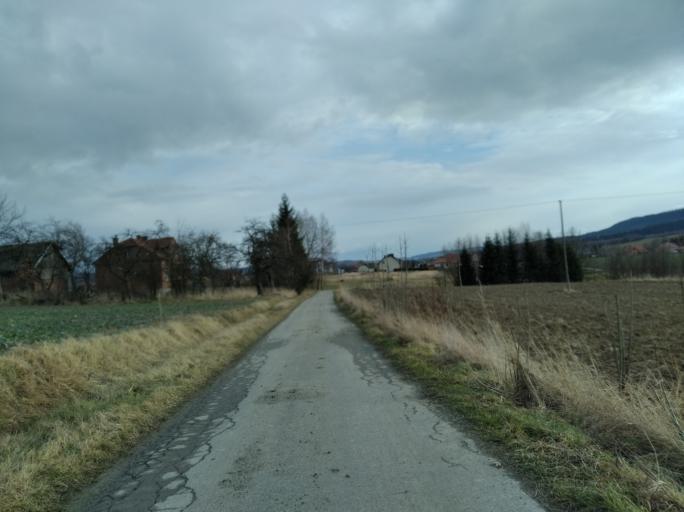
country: PL
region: Subcarpathian Voivodeship
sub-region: Powiat strzyzowski
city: Strzyzow
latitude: 49.8521
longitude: 21.7726
